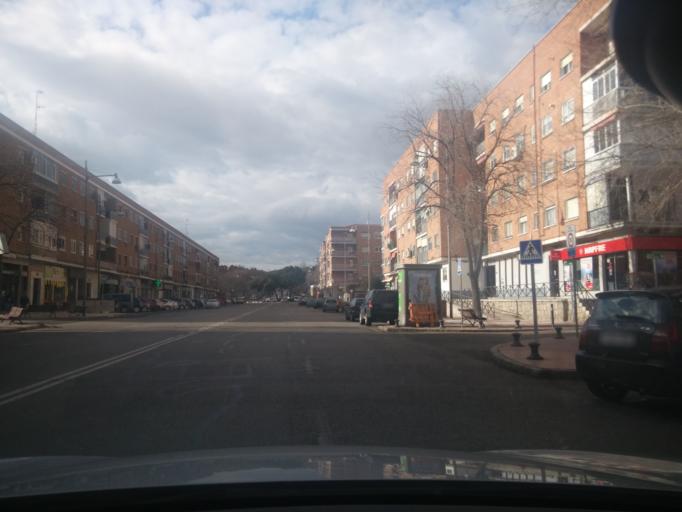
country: ES
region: Madrid
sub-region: Provincia de Madrid
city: Alcobendas
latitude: 40.5440
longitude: -3.6412
